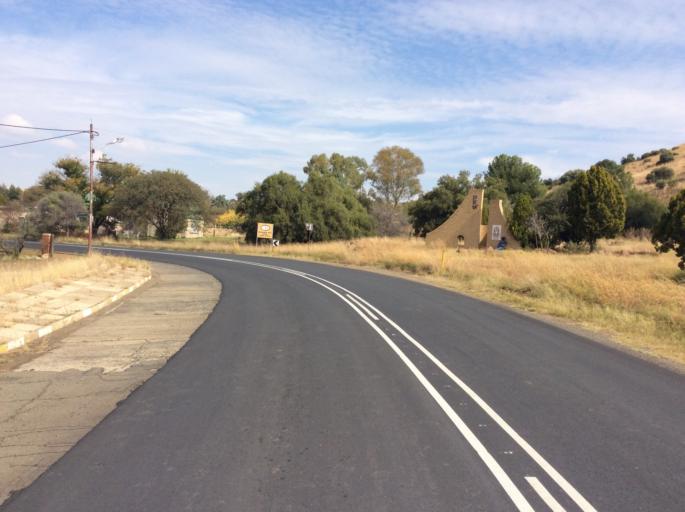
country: ZA
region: Orange Free State
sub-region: Xhariep District Municipality
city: Dewetsdorp
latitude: -29.5788
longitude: 26.6625
